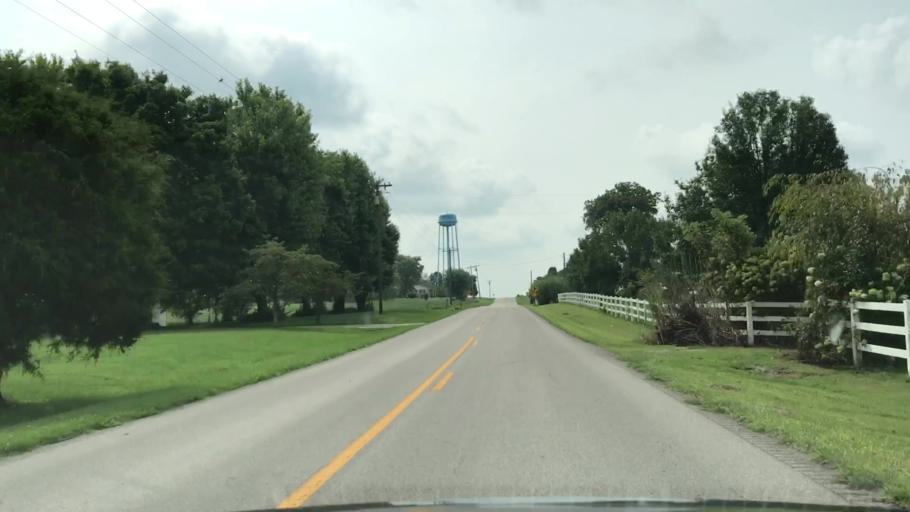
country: US
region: Kentucky
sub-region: Edmonson County
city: Brownsville
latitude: 37.1155
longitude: -86.1508
